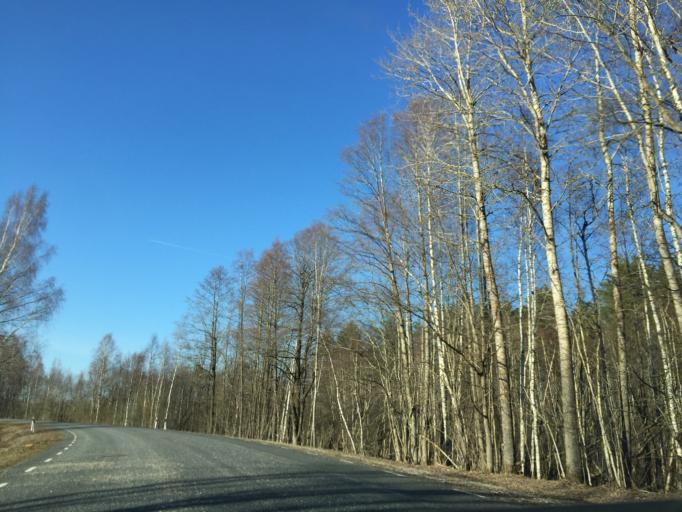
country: RU
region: Pskov
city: Gdov
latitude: 59.0195
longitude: 27.6904
